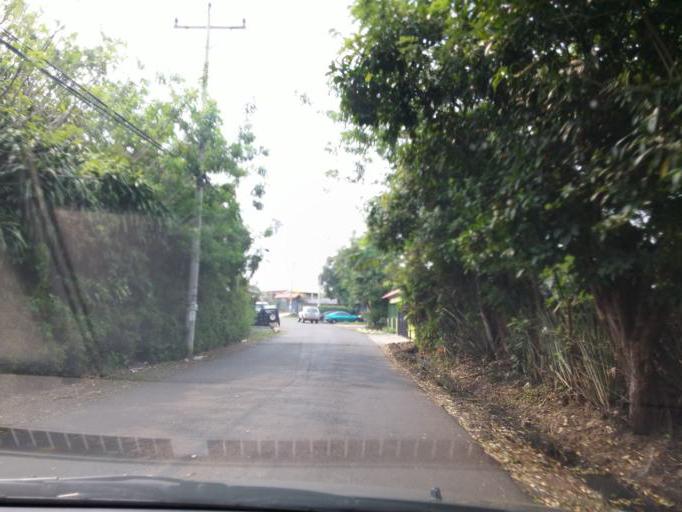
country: CR
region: Alajuela
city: Alajuela
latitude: 9.9881
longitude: -84.2269
